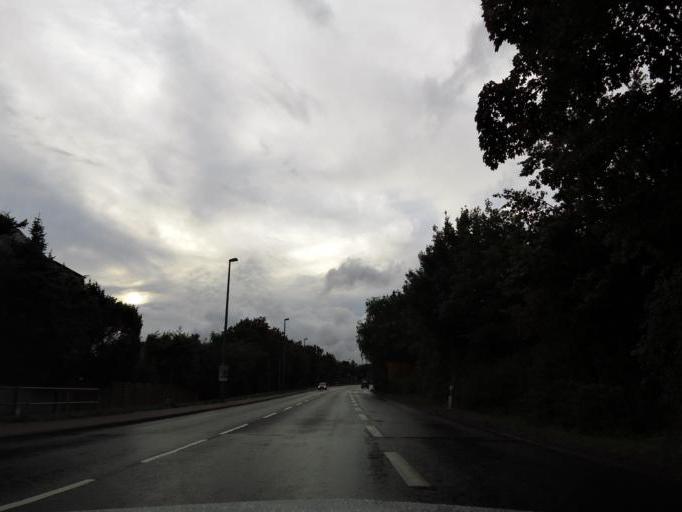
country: DE
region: Hesse
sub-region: Regierungsbezirk Darmstadt
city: Bad Homburg vor der Hoehe
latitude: 50.1852
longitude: 8.6521
